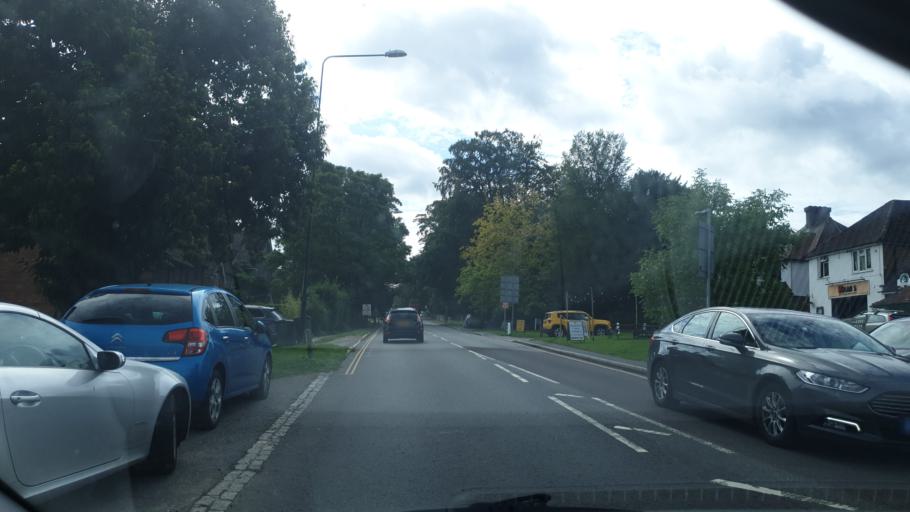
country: GB
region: England
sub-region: East Sussex
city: Forest Row
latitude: 51.0977
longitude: 0.0334
